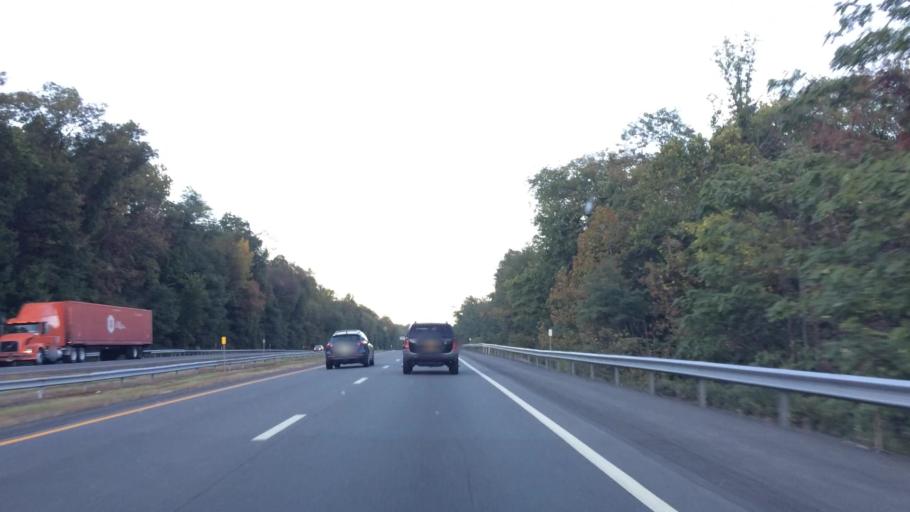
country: US
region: New York
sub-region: Orange County
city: Woodbury
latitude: 41.3858
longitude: -74.0994
